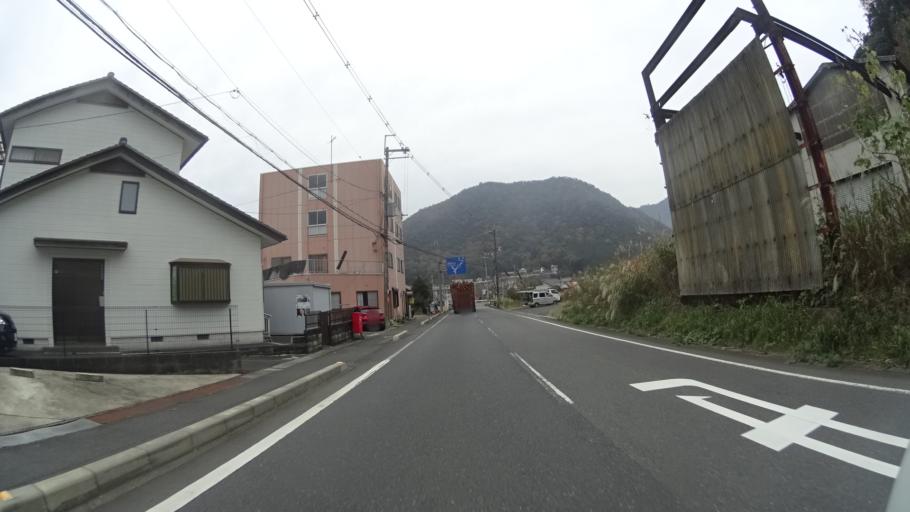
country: JP
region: Kyoto
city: Maizuru
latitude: 35.4992
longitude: 135.4334
